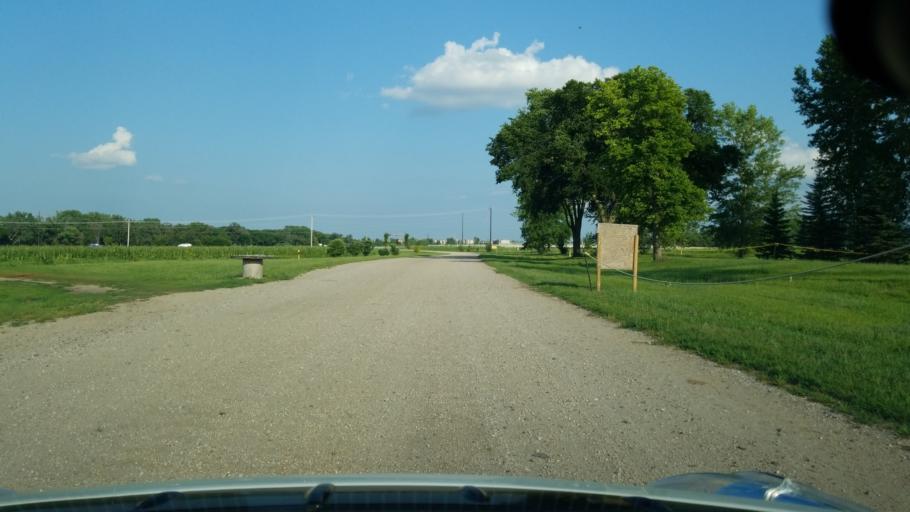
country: US
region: Nebraska
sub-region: Sarpy County
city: Papillion
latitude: 41.1509
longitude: -95.9890
